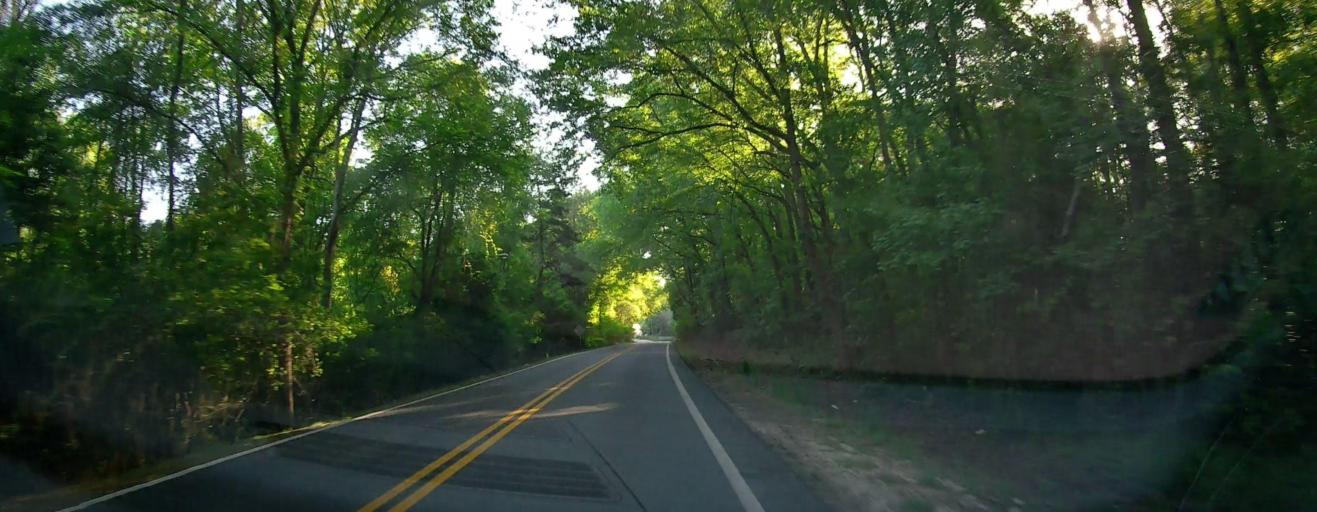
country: US
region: Georgia
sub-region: Macon County
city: Montezuma
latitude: 32.3091
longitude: -84.0165
